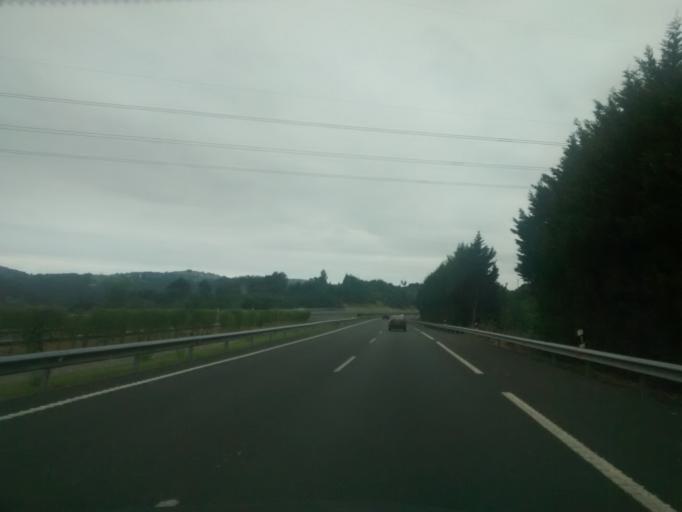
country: ES
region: Cantabria
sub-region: Provincia de Cantabria
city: Luzmela
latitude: 43.3322
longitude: -4.1592
